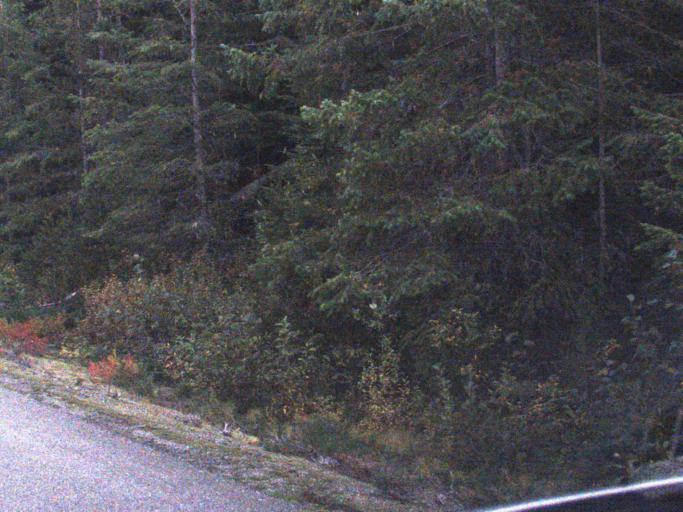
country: US
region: Washington
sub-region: Snohomish County
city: Darrington
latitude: 48.6590
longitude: -120.8614
